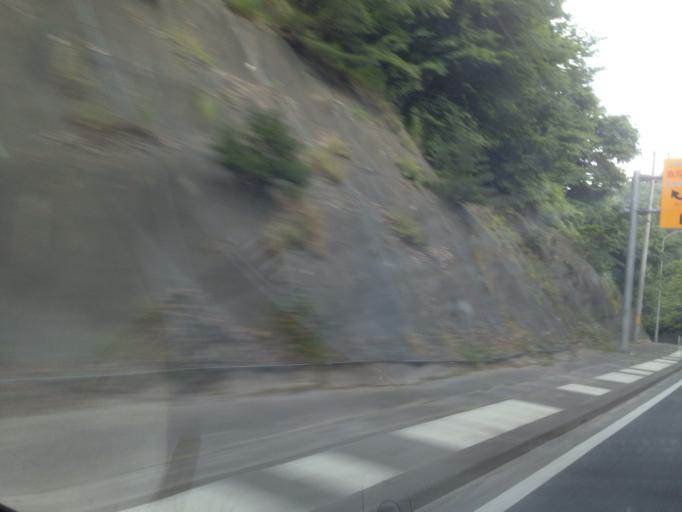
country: JP
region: Iwate
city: Kamaishi
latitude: 39.3155
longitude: 141.8844
